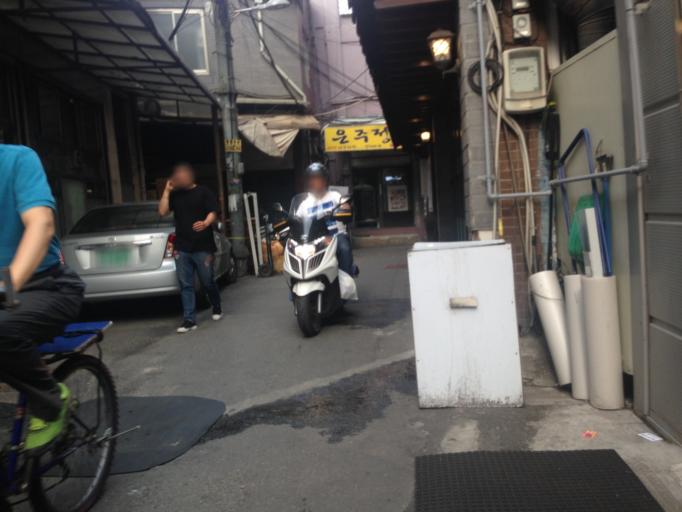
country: KR
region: Seoul
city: Seoul
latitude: 37.5688
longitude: 126.9994
